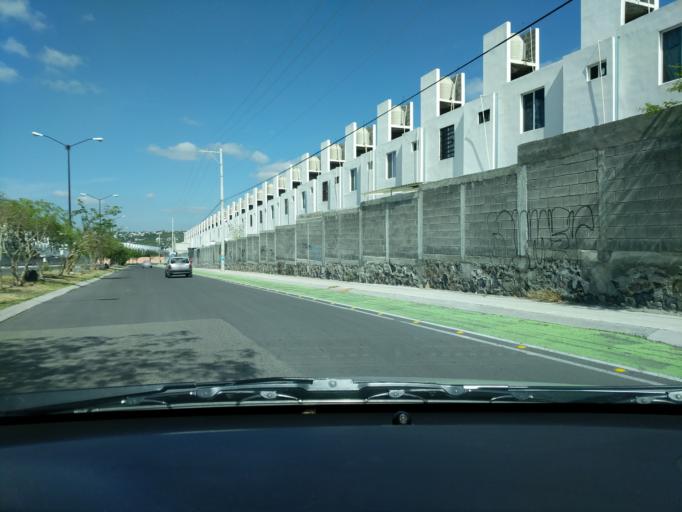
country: MX
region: Queretaro
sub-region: Queretaro
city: Patria Nueva
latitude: 20.6399
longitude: -100.4807
